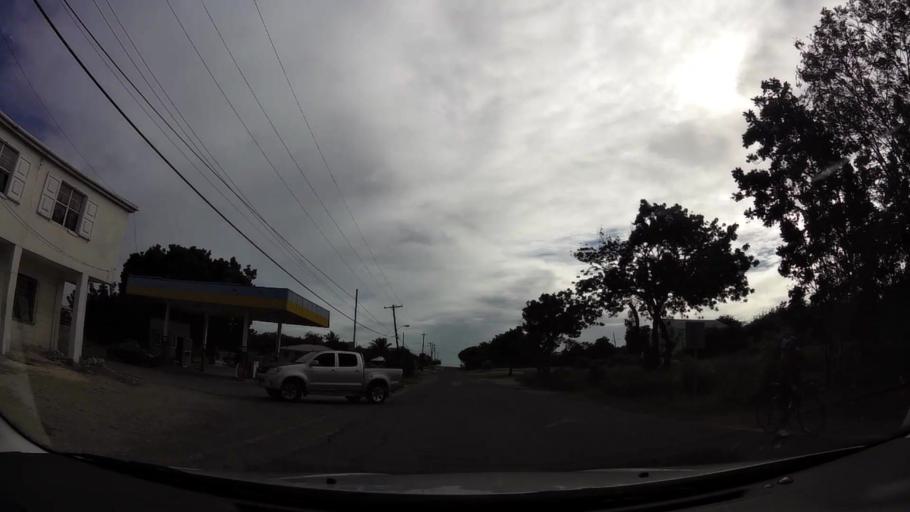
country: AG
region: Saint Peter
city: Parham
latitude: 17.0846
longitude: -61.7236
